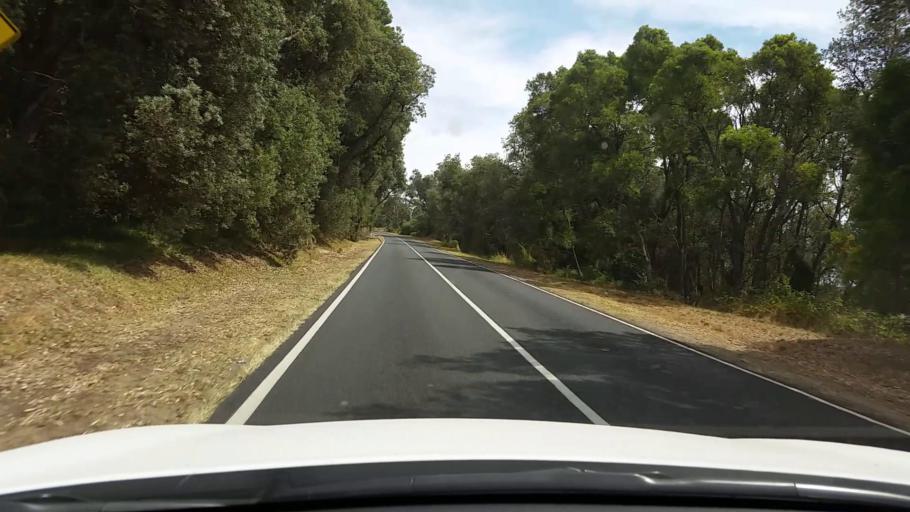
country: AU
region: Victoria
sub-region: Mornington Peninsula
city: Saint Andrews Beach
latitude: -38.4714
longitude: 144.9250
